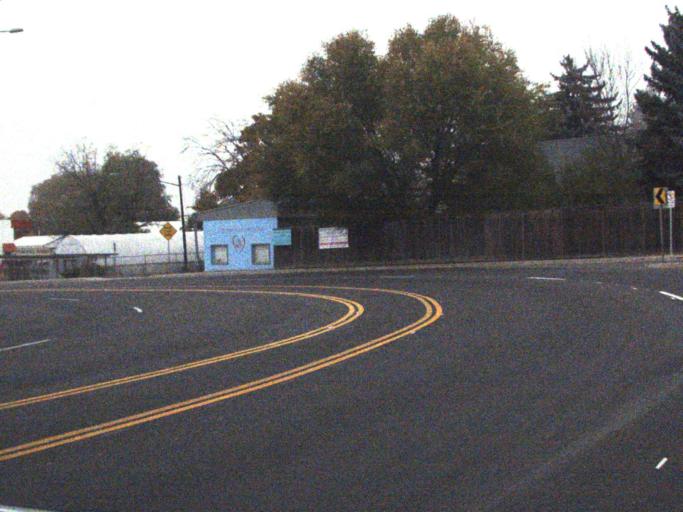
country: US
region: Washington
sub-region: Stevens County
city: Colville
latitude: 48.5483
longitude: -117.9062
